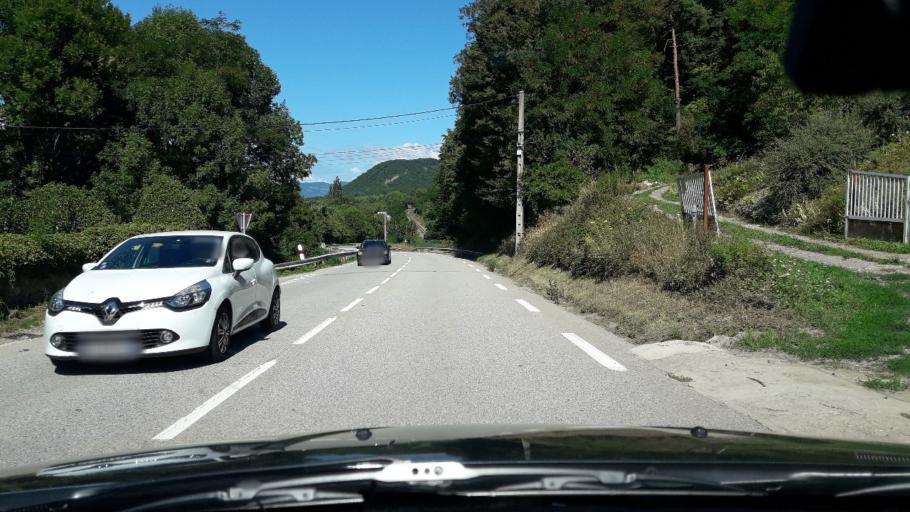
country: FR
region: Rhone-Alpes
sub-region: Departement de l'Isere
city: Vif
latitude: 45.0360
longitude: 5.6686
